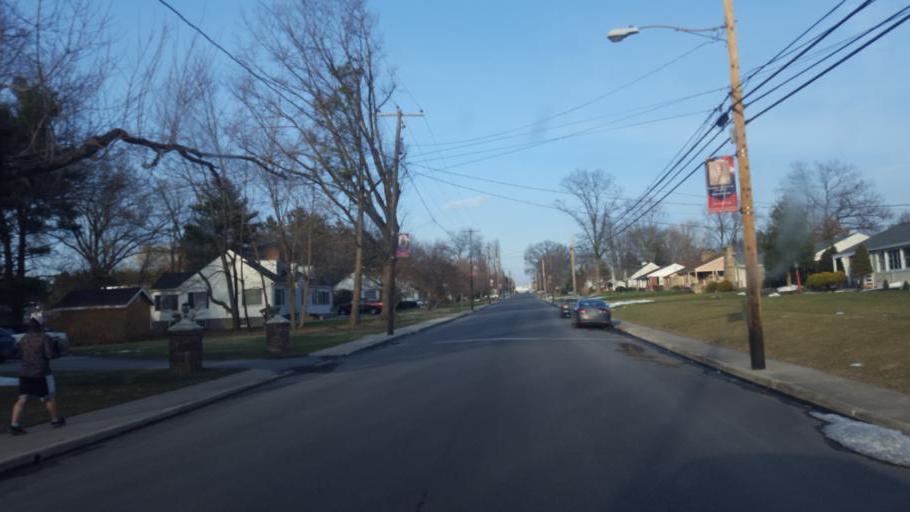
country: US
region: Pennsylvania
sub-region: Lancaster County
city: New Holland
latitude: 40.1045
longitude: -76.0729
